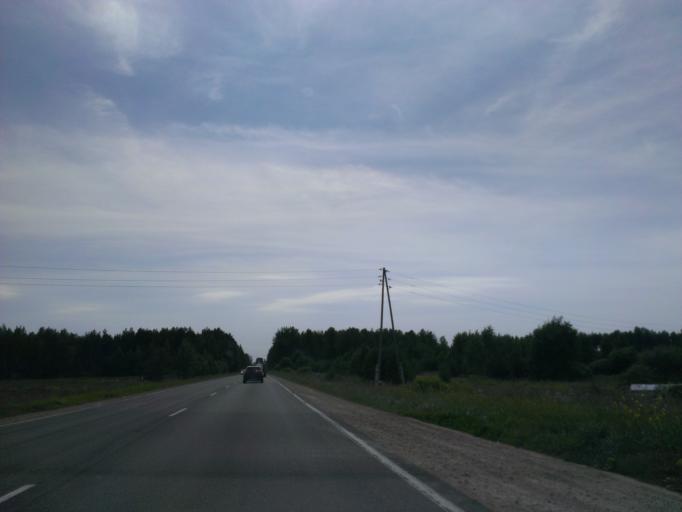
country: LV
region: Salaspils
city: Salaspils
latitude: 56.8967
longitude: 24.4068
